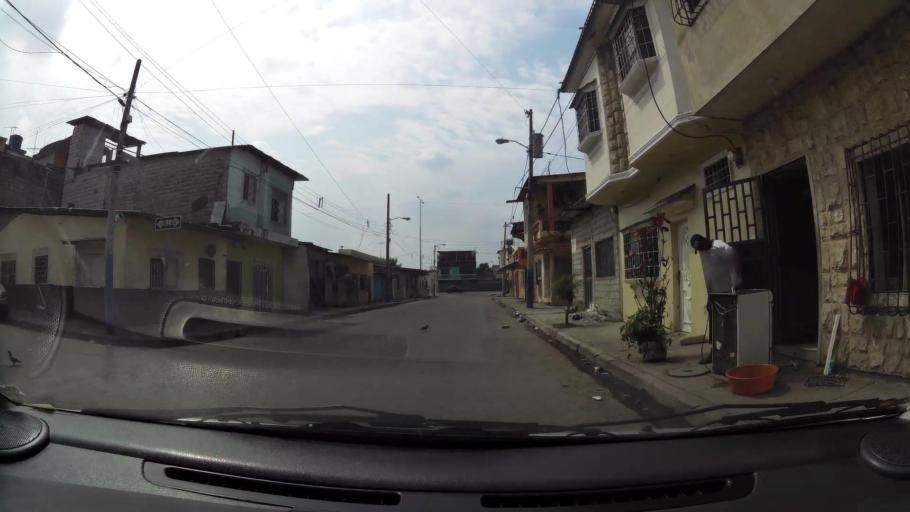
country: EC
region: Guayas
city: Guayaquil
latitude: -2.2398
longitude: -79.9080
